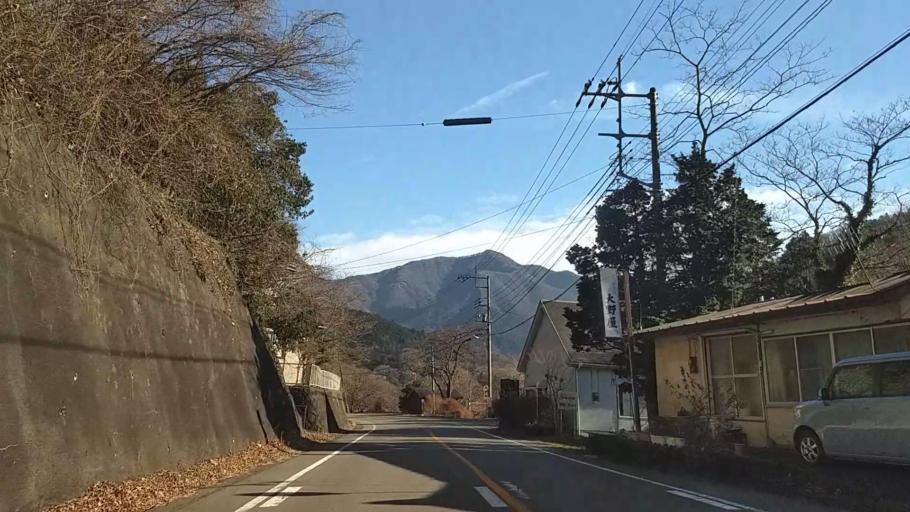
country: JP
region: Yamanashi
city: Uenohara
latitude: 35.5357
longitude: 139.0884
